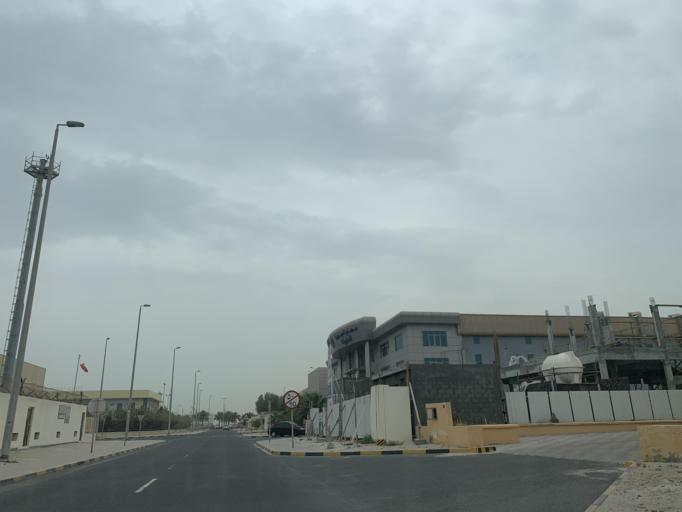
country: BH
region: Muharraq
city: Al Hadd
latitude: 26.2239
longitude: 50.6673
